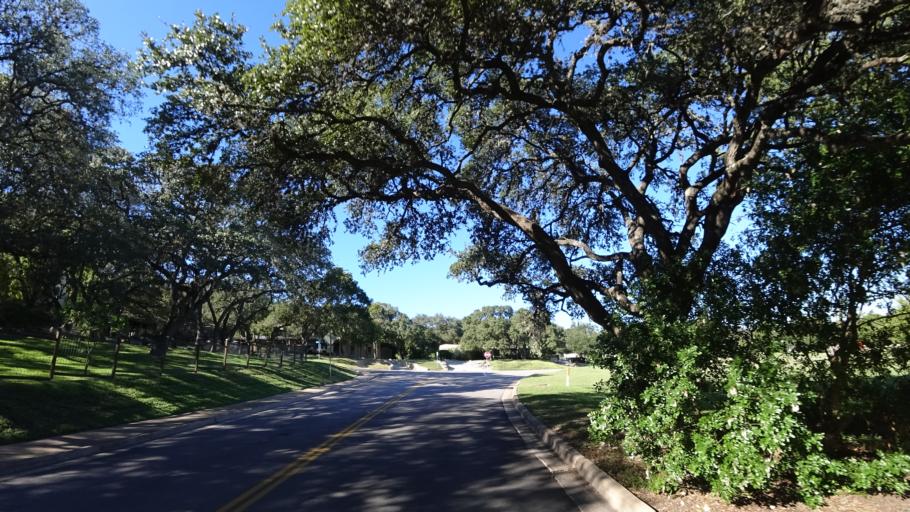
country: US
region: Texas
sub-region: Travis County
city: West Lake Hills
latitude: 30.3312
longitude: -97.7629
